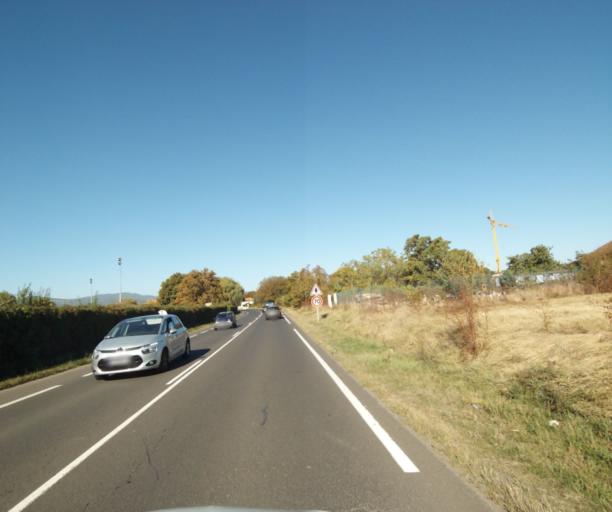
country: FR
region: Auvergne
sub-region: Departement du Puy-de-Dome
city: Gerzat
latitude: 45.8255
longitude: 3.1304
